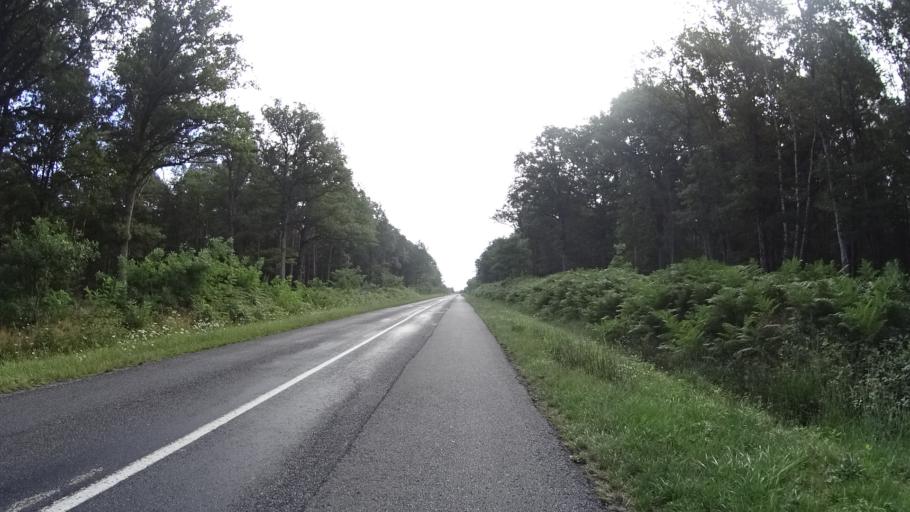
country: FR
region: Centre
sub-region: Departement du Loiret
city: Bouzy-la-Foret
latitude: 47.8670
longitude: 2.4069
